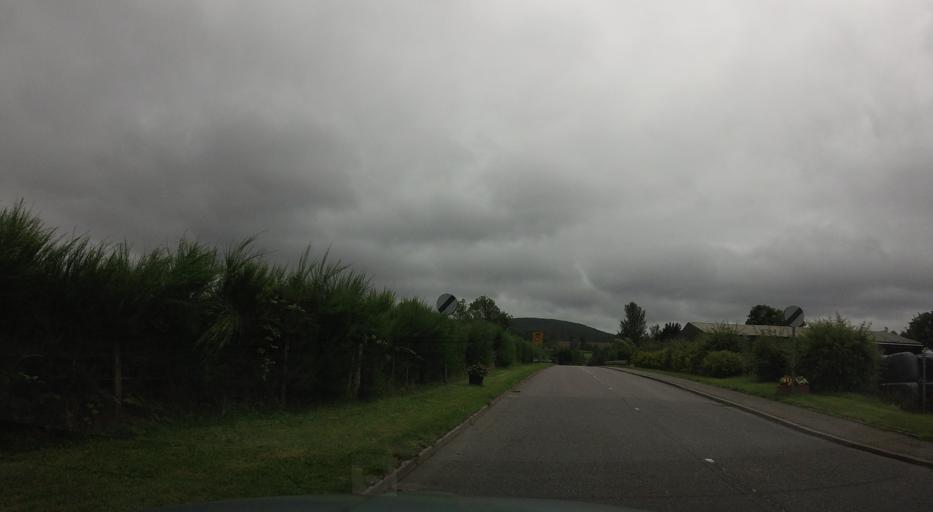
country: GB
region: Scotland
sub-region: Aberdeenshire
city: Banchory
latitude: 57.0205
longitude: -2.5360
